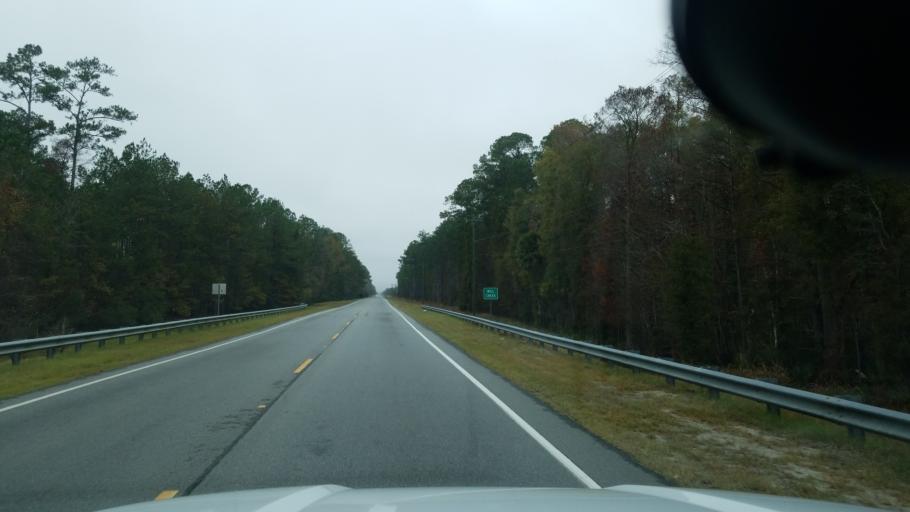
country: US
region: Georgia
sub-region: Charlton County
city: Folkston
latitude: 30.8328
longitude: -81.8812
